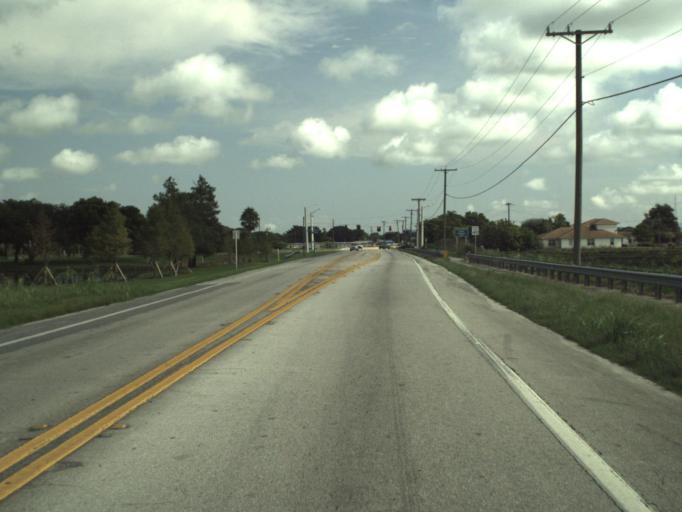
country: US
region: Florida
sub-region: Palm Beach County
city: Belle Glade Camp
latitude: 26.6743
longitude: -80.6866
